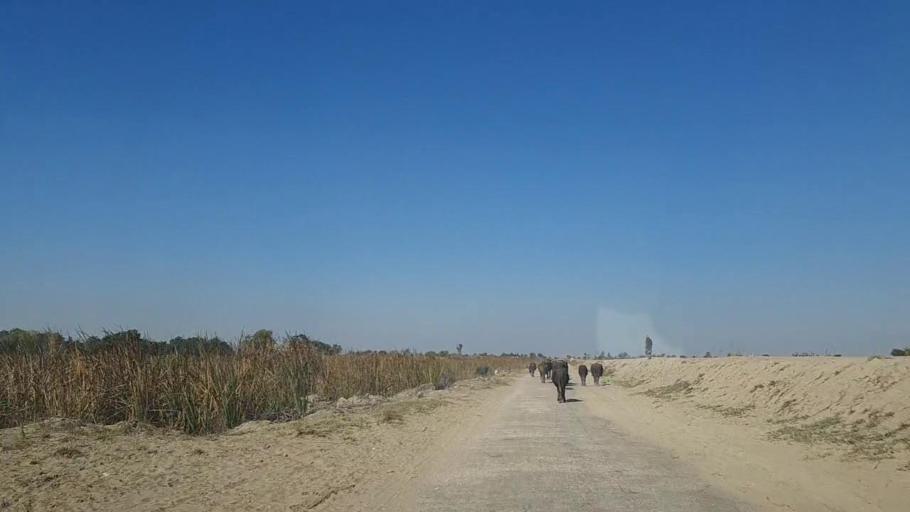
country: PK
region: Sindh
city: Sanghar
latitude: 26.2116
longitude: 68.9293
